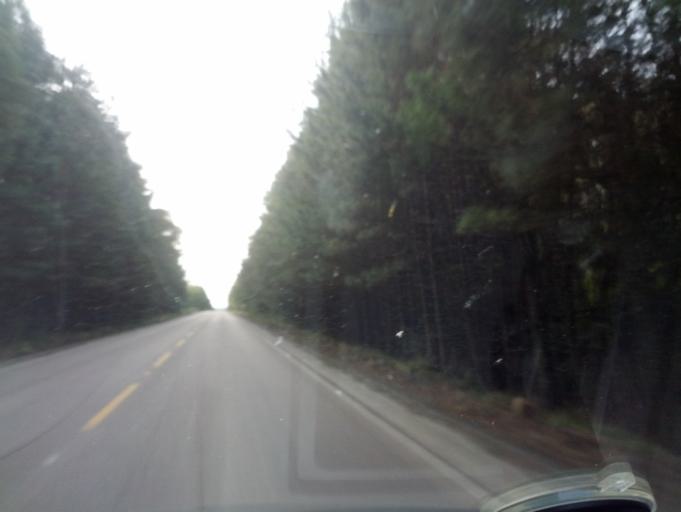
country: BR
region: Santa Catarina
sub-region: Otacilio Costa
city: Otacilio Costa
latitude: -27.3770
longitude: -50.1345
